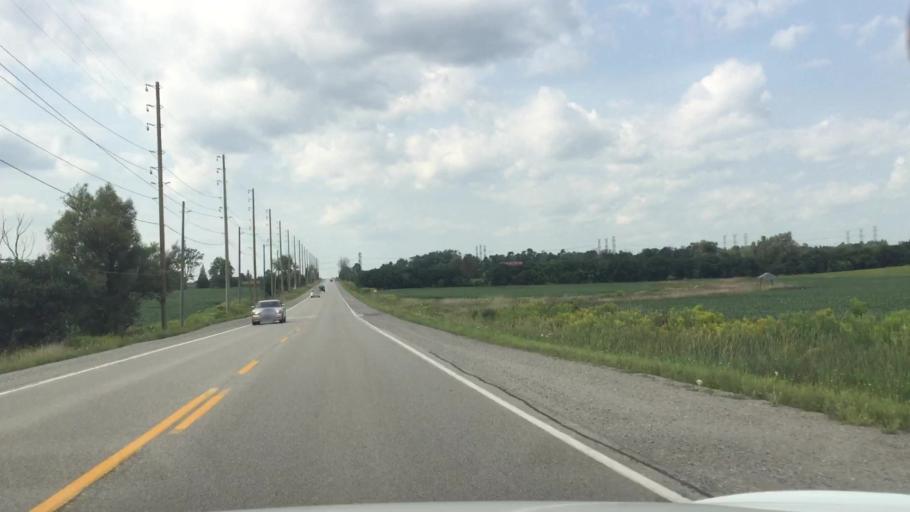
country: CA
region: Ontario
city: Oshawa
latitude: 43.9650
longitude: -78.8607
